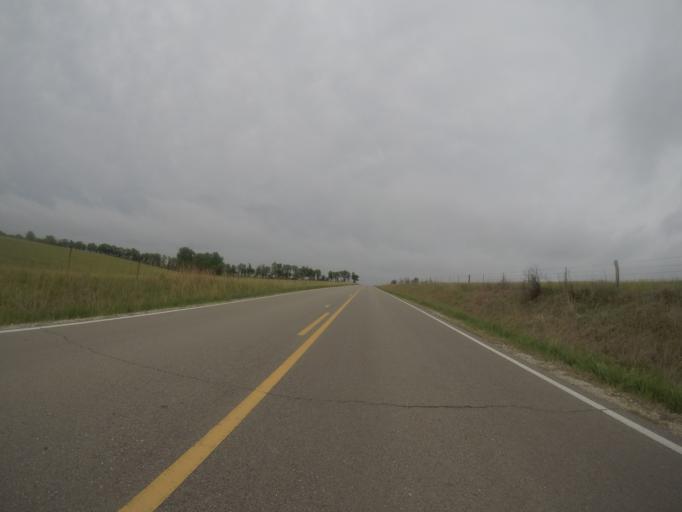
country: US
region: Kansas
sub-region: Pottawatomie County
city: Westmoreland
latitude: 39.5172
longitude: -96.2395
